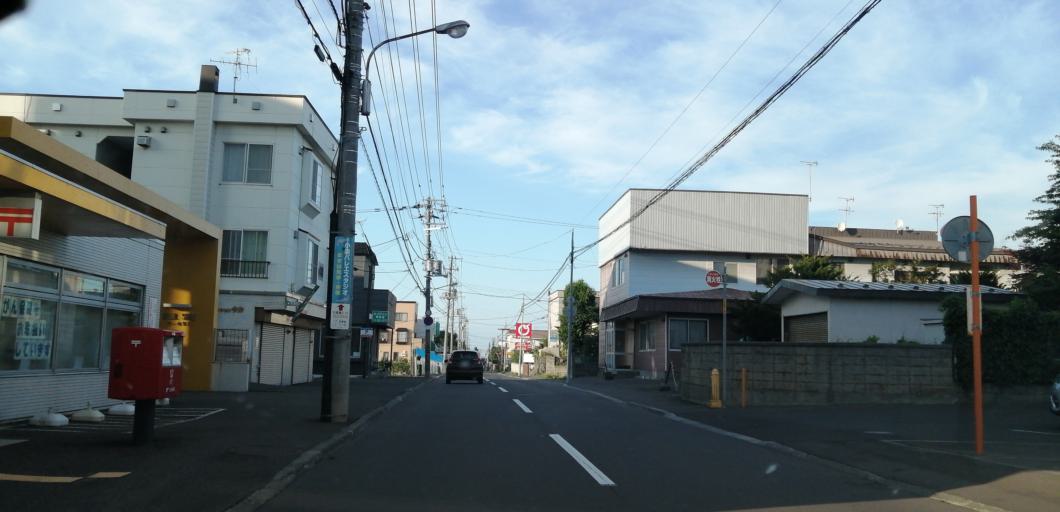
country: JP
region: Hokkaido
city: Sapporo
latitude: 43.0139
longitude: 141.4197
